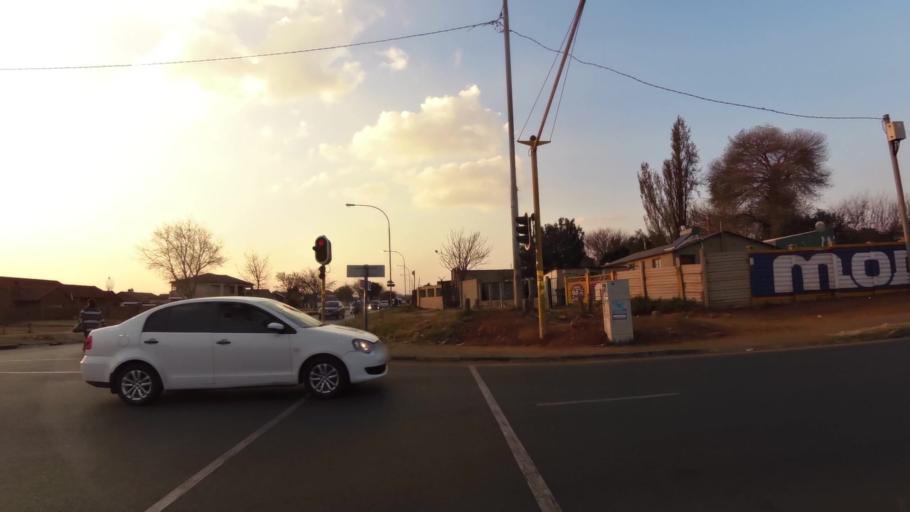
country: ZA
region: Gauteng
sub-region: City of Johannesburg Metropolitan Municipality
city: Soweto
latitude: -26.2913
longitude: 27.8908
